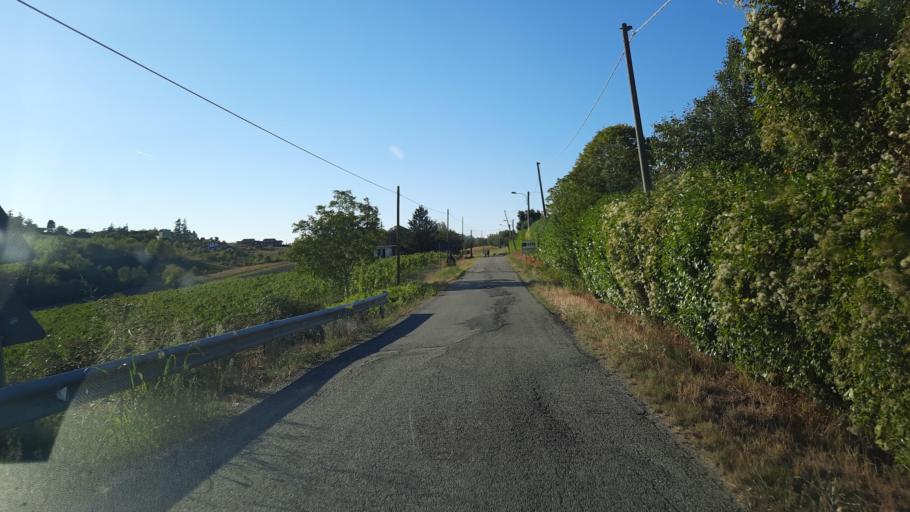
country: IT
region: Piedmont
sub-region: Provincia di Alessandria
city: Camagna Monferrato
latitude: 44.9987
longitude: 8.4294
